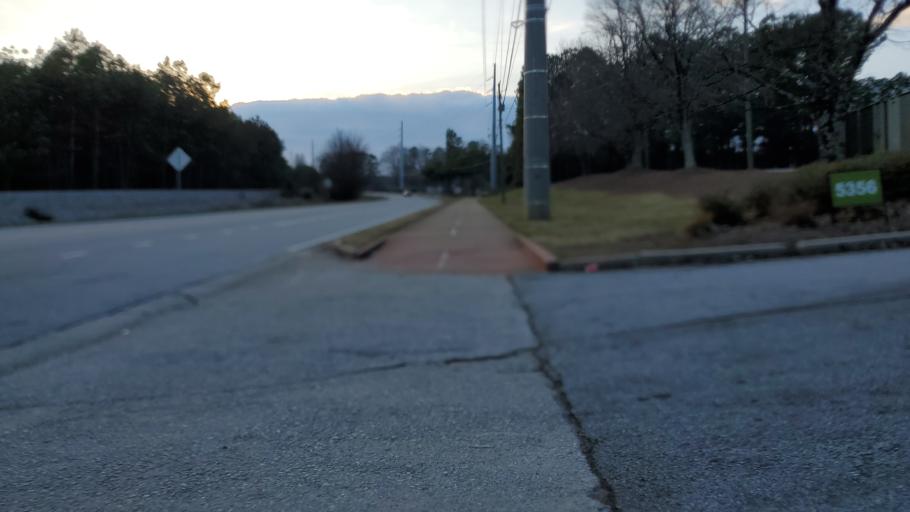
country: US
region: Georgia
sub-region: DeKalb County
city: Tucker
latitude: 33.8257
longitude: -84.1994
